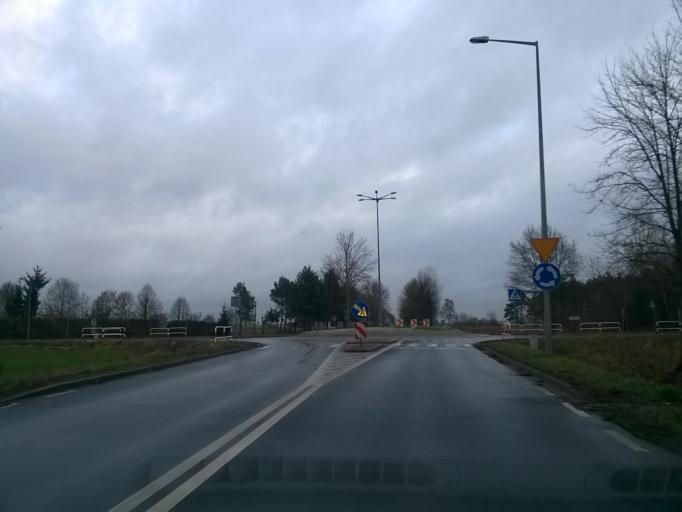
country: PL
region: Greater Poland Voivodeship
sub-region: Powiat wagrowiecki
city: Golancz
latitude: 52.9135
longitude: 17.3669
